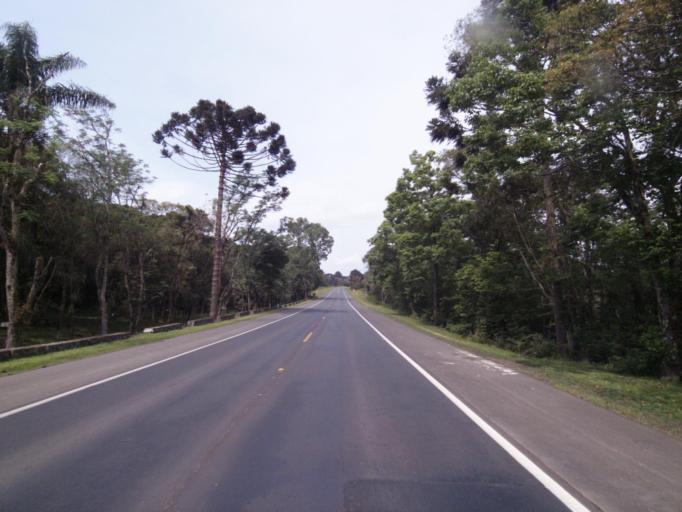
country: BR
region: Parana
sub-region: Irati
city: Irati
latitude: -25.4668
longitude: -50.5181
